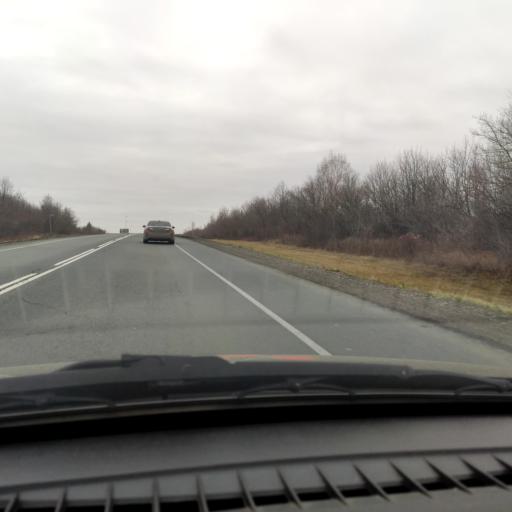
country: RU
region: Samara
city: Zhigulevsk
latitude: 53.3507
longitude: 49.4527
